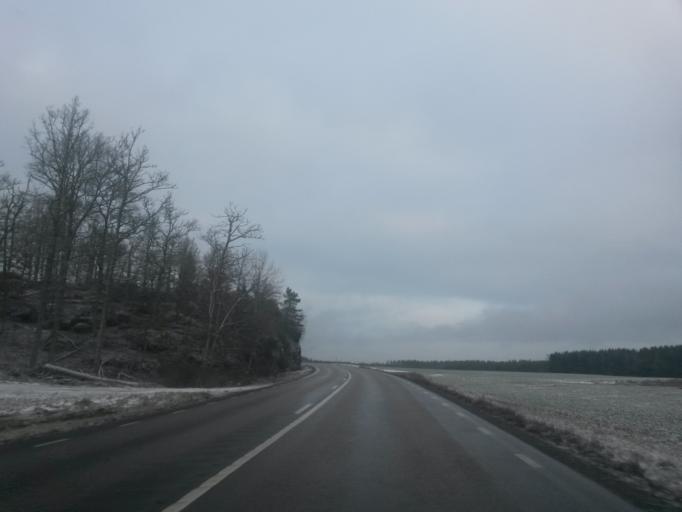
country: SE
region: Vaestra Goetaland
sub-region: Vargarda Kommun
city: Jonstorp
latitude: 58.0925
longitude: 12.6593
